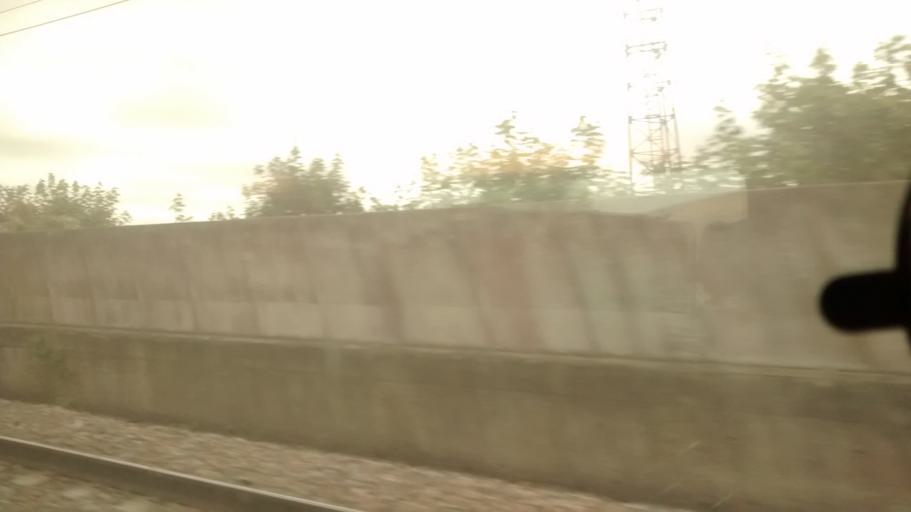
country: FR
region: Centre
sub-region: Departement d'Eure-et-Loir
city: Beville-le-Comte
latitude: 48.3924
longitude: 1.7325
